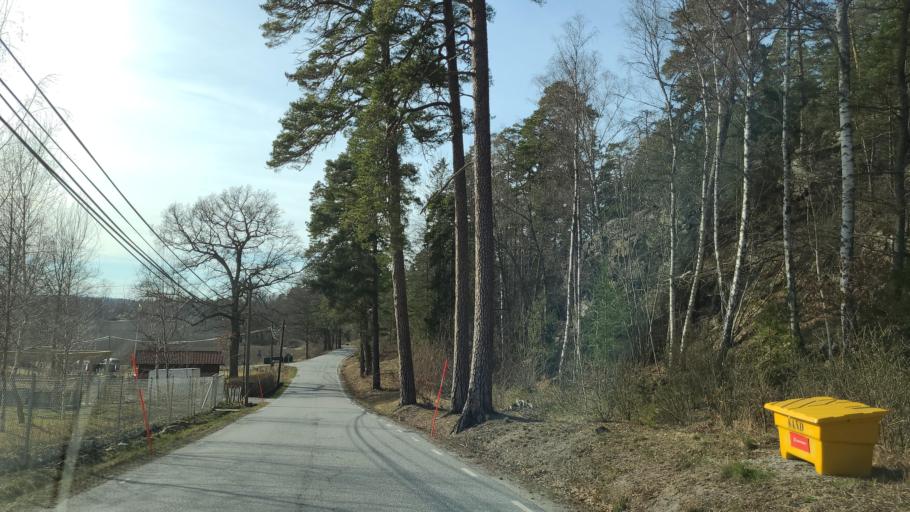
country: SE
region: Stockholm
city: Stenhamra
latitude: 59.2775
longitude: 17.6821
